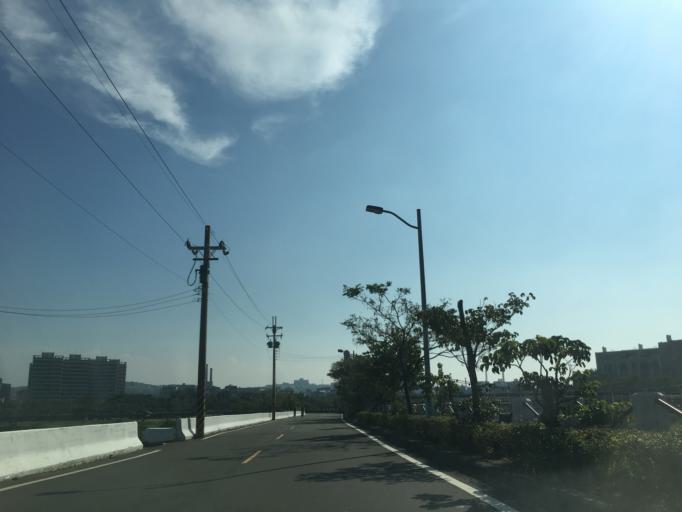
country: TW
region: Taiwan
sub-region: Hsinchu
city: Hsinchu
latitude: 24.8023
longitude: 120.9364
